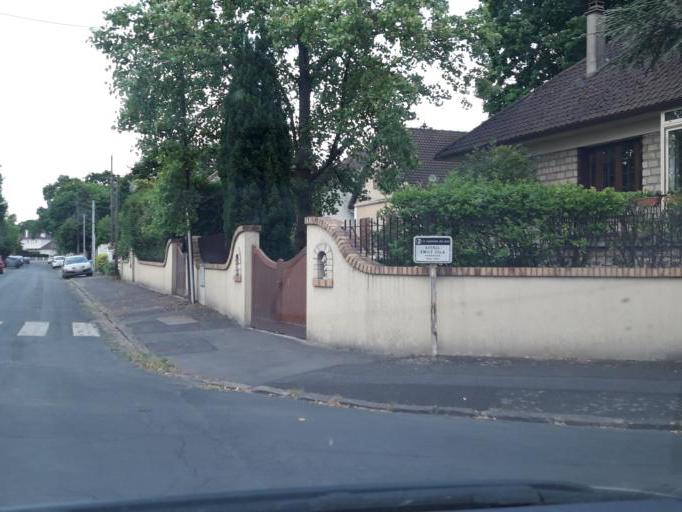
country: FR
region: Ile-de-France
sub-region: Departement de l'Essonne
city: Villemoisson-sur-Orge
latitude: 48.6470
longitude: 2.3398
